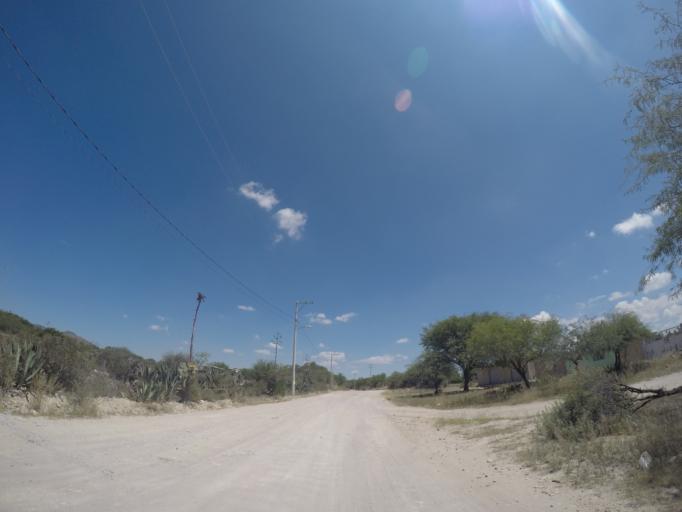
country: MX
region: San Luis Potosi
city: La Pila
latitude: 21.9970
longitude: -100.8986
